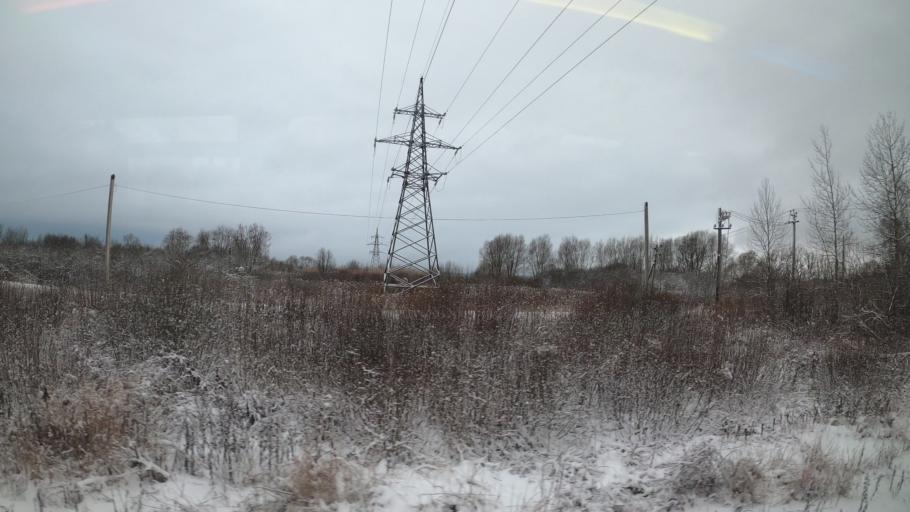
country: RU
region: Jaroslavl
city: Pereslavl'-Zalesskiy
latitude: 56.7313
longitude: 38.9006
